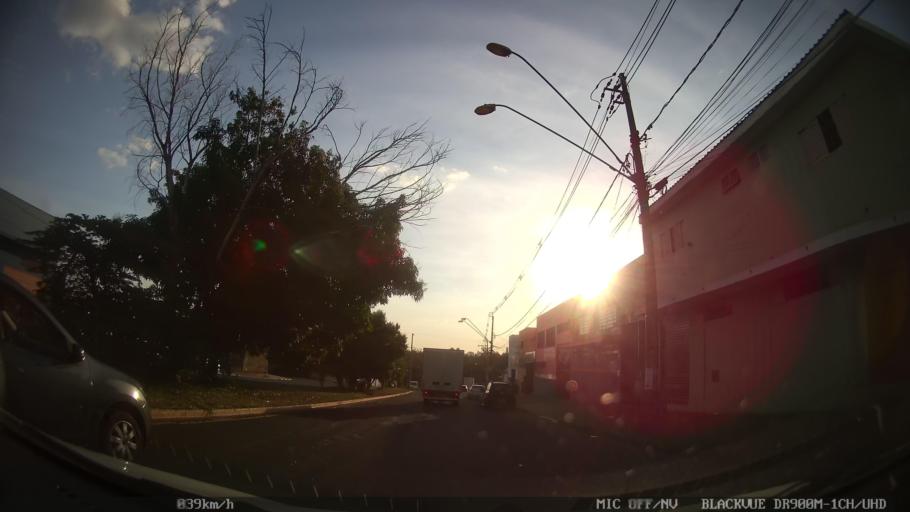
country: BR
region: Sao Paulo
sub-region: Ribeirao Preto
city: Ribeirao Preto
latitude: -21.1374
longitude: -47.7997
